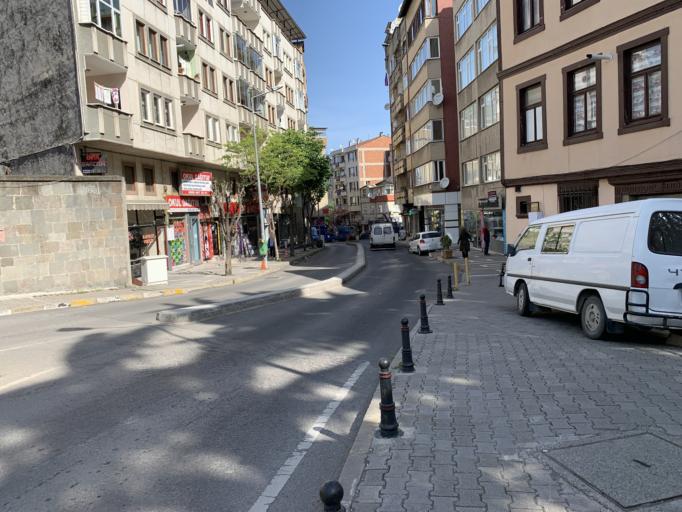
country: TR
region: Trabzon
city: Trabzon
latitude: 41.0039
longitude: 39.7240
